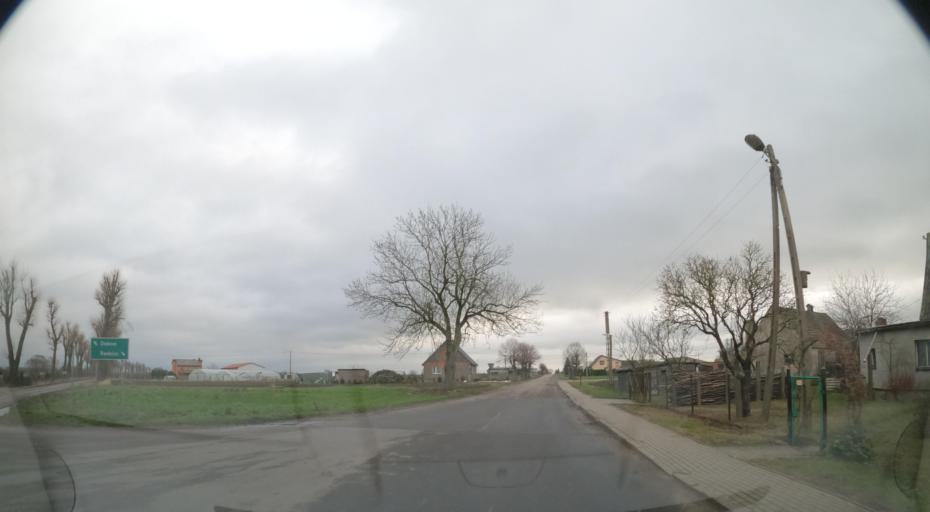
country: PL
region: Greater Poland Voivodeship
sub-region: Powiat pilski
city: Lobzenica
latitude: 53.2293
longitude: 17.3236
